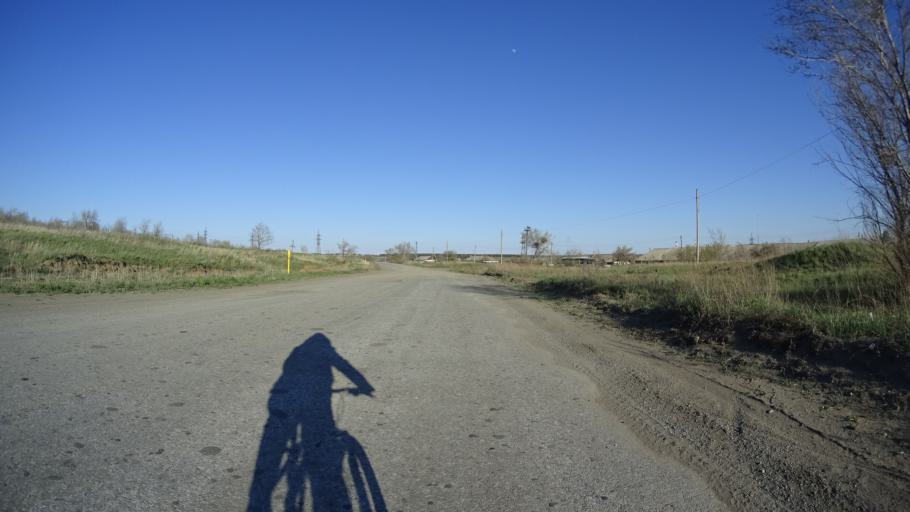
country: RU
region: Chelyabinsk
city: Troitsk
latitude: 54.0769
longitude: 61.6017
